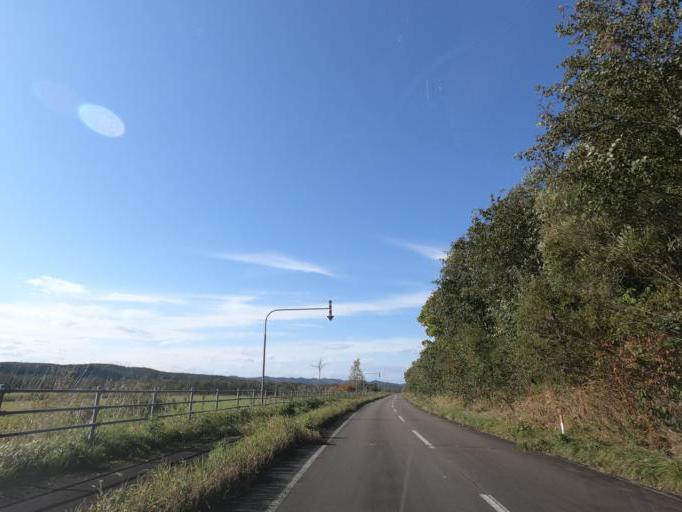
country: JP
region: Hokkaido
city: Obihiro
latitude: 42.6300
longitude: 143.5251
